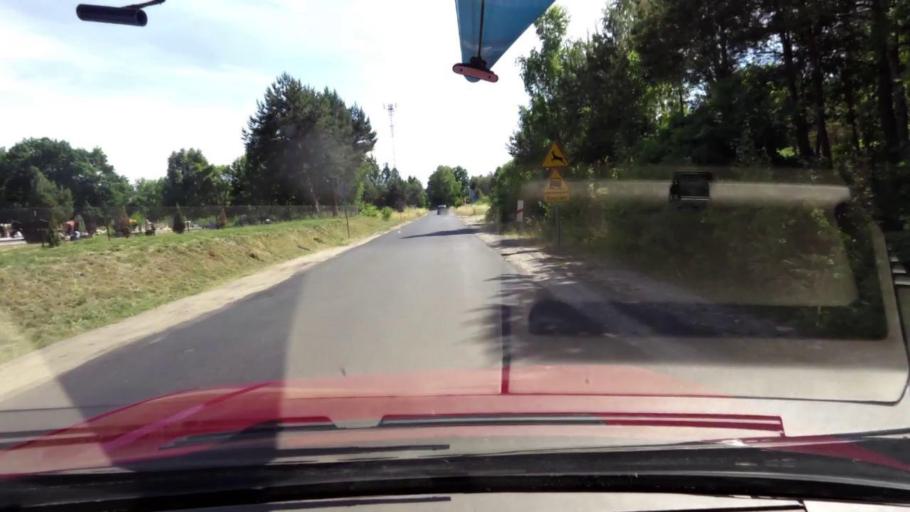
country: PL
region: Pomeranian Voivodeship
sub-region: Powiat slupski
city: Kepice
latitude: 54.2862
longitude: 16.9589
